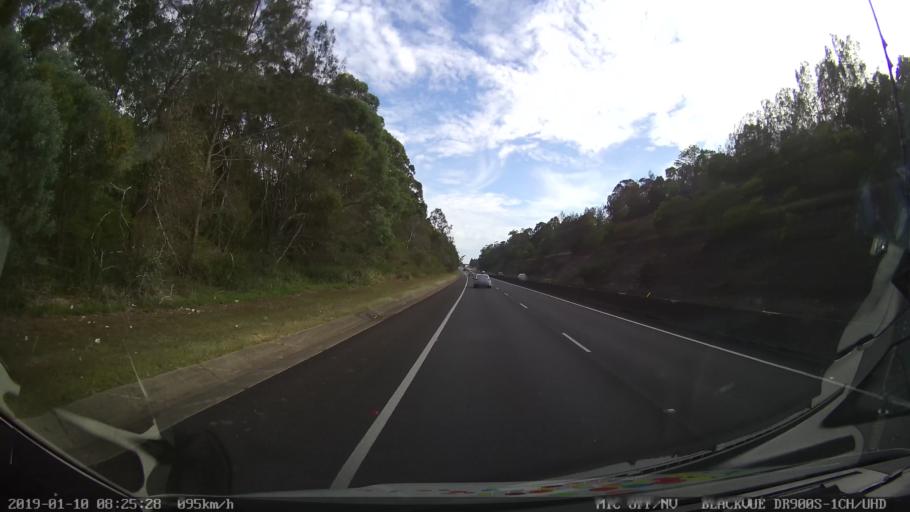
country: AU
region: New South Wales
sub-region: Coffs Harbour
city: Bonville
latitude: -30.4335
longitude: 153.0171
